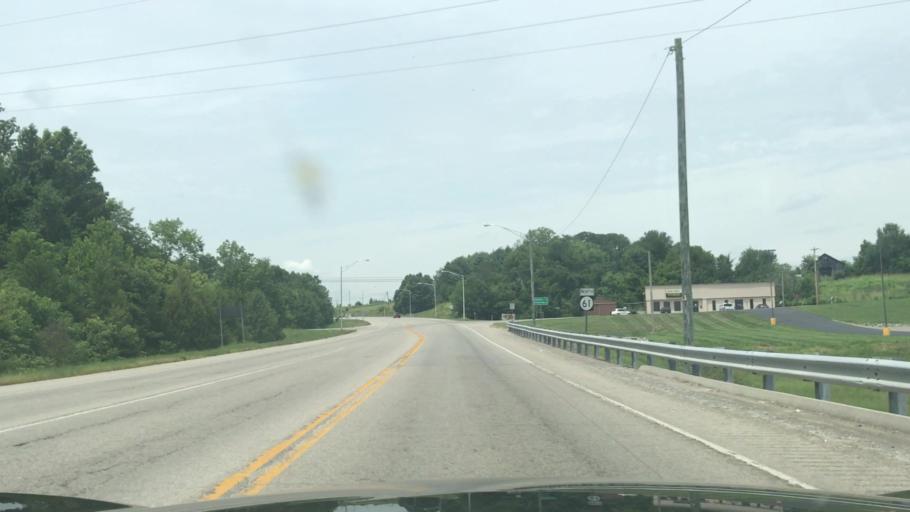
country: US
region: Kentucky
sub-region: Green County
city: Greensburg
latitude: 37.2714
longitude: -85.4968
